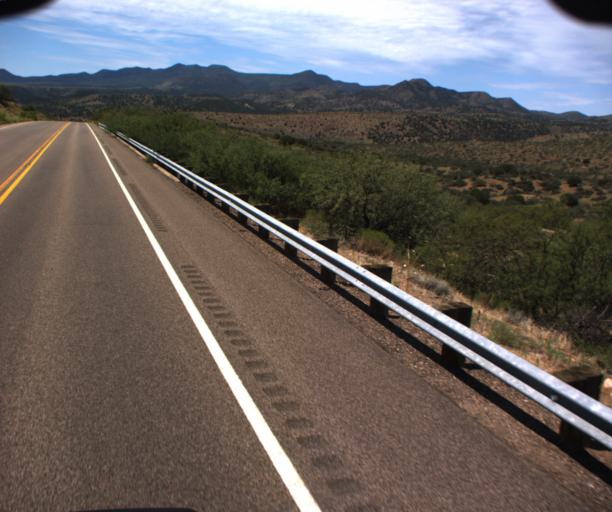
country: US
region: Arizona
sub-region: Gila County
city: Globe
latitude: 33.5991
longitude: -110.6357
